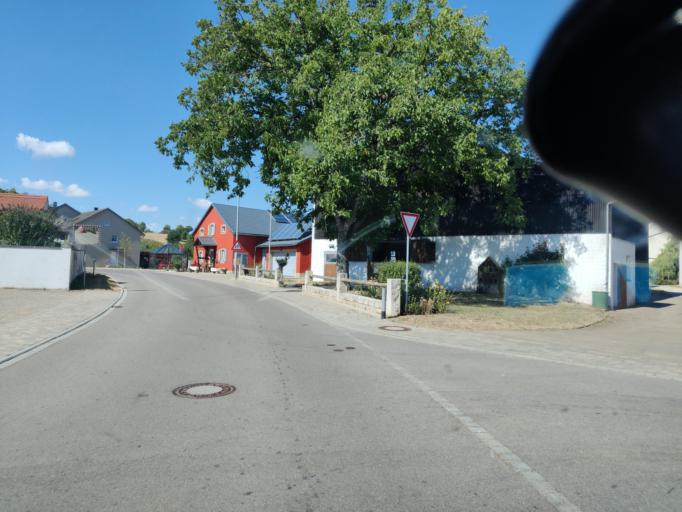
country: DE
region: Bavaria
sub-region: Regierungsbezirk Mittelfranken
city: Bergen
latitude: 49.0718
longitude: 11.0884
